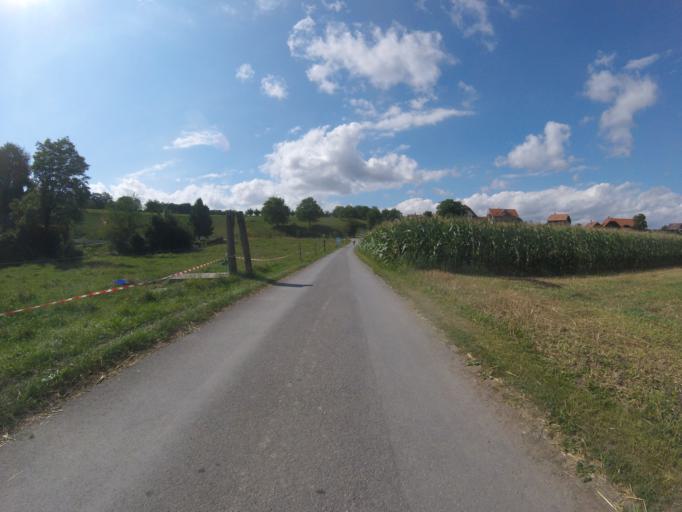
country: CH
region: Bern
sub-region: Bern-Mittelland District
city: Kehrsatz
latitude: 46.9183
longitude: 7.4805
